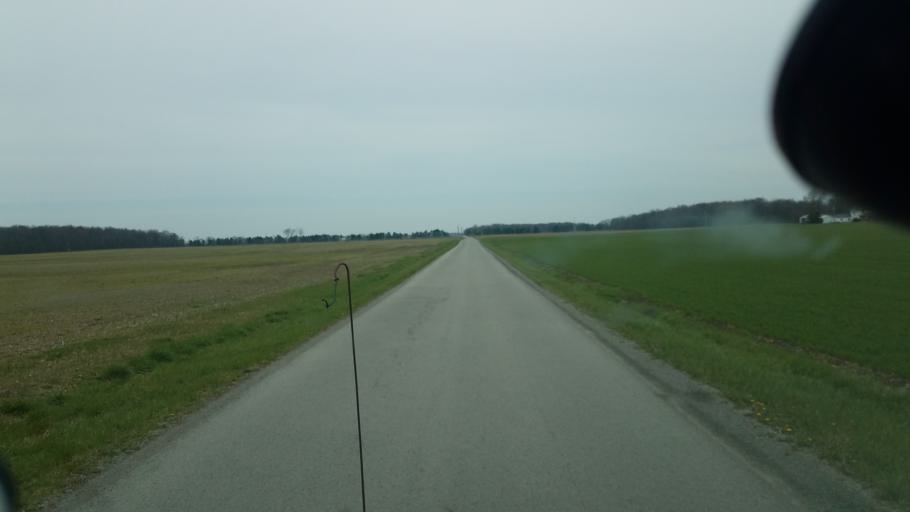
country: US
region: Ohio
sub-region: Wyandot County
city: Carey
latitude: 40.9721
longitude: -83.5131
